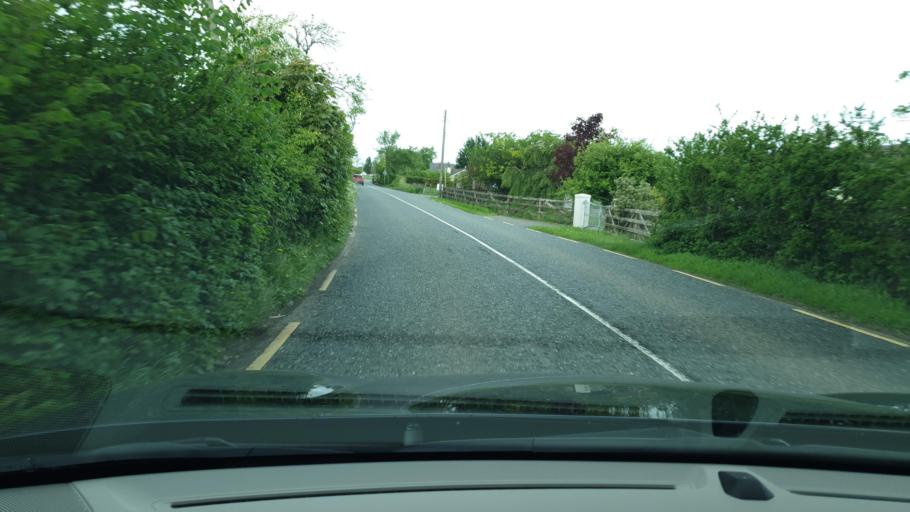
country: IE
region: Leinster
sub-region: An Mhi
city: Ratoath
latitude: 53.5289
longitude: -6.4505
